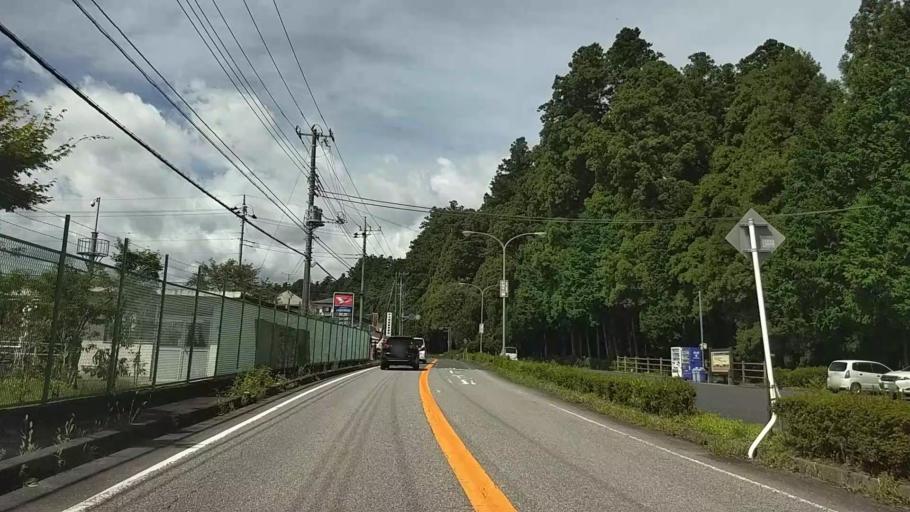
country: JP
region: Tochigi
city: Imaichi
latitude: 36.7277
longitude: 139.6783
